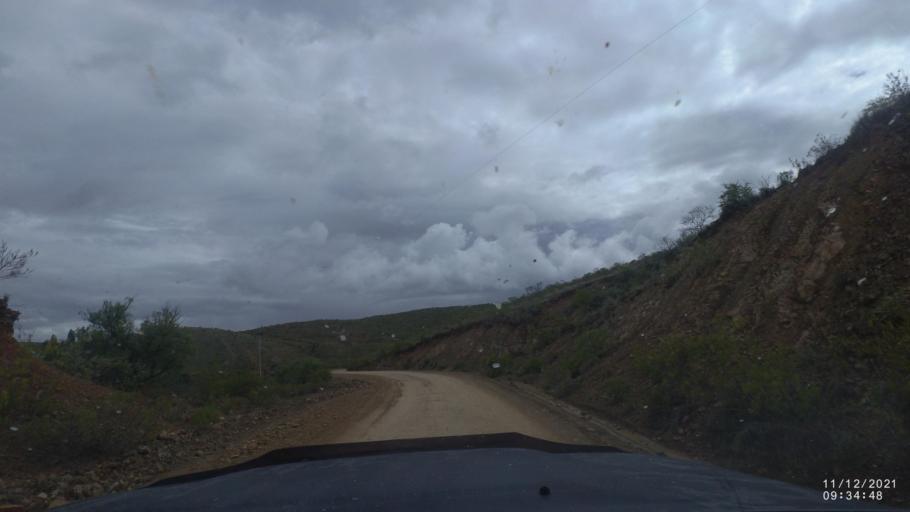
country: BO
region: Cochabamba
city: Tarata
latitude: -17.8307
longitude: -65.9910
